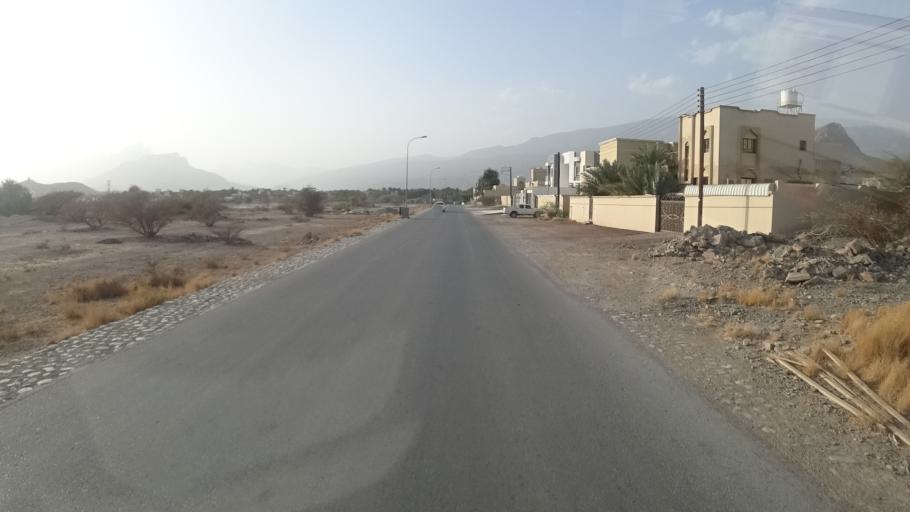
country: OM
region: Muhafazat ad Dakhiliyah
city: Bahla'
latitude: 23.0922
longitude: 57.3119
